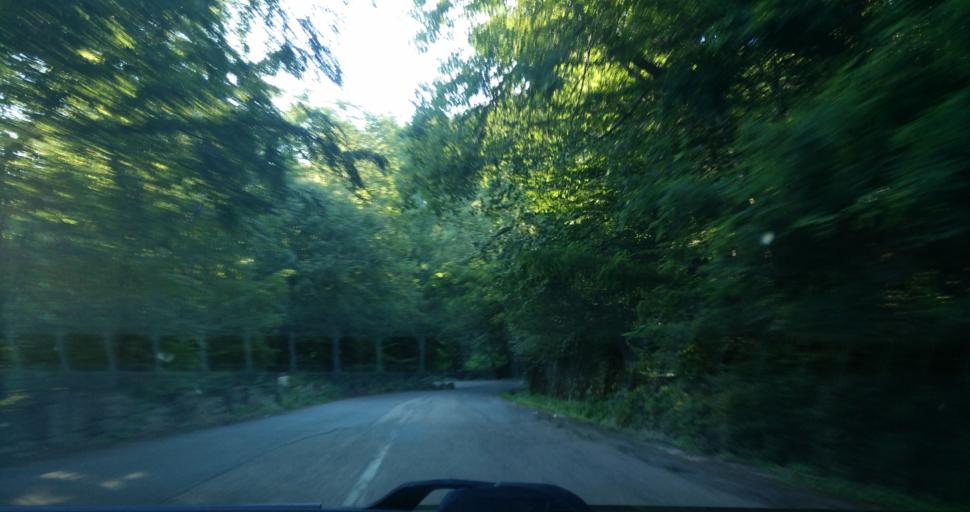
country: RO
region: Bihor
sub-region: Oras Nucet
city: Nucet
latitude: 46.4883
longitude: 22.6098
